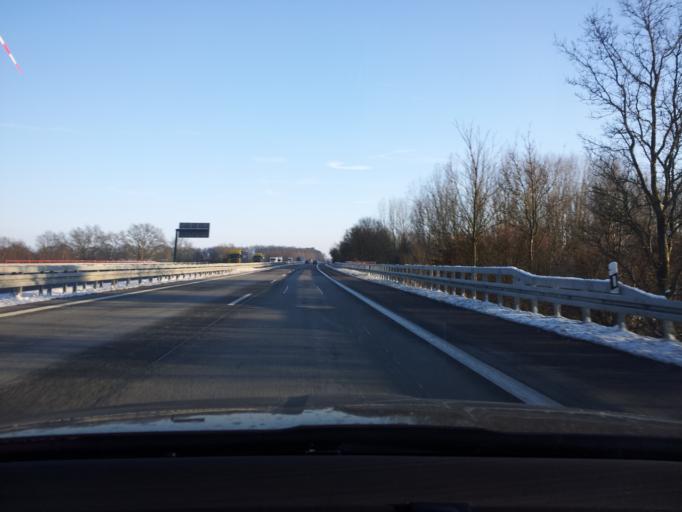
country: DE
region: Brandenburg
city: Gerdshagen
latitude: 53.2297
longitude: 12.2136
